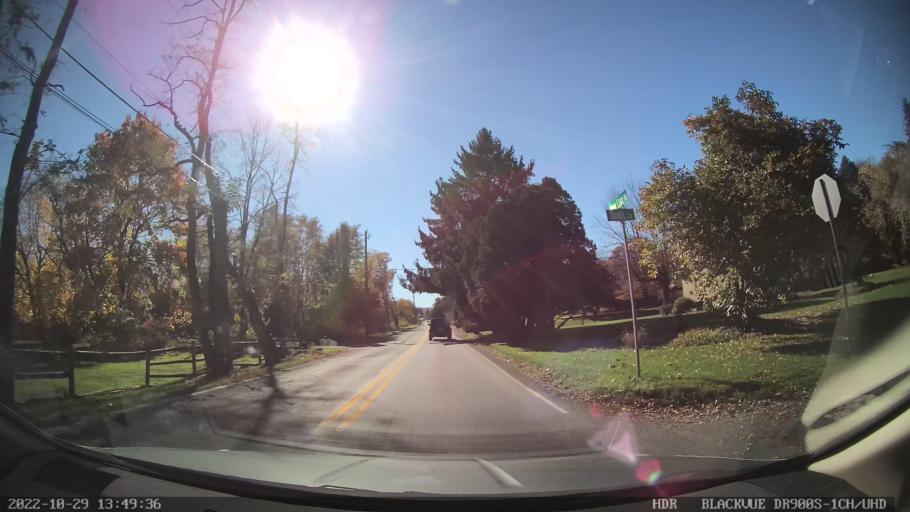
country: US
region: Pennsylvania
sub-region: Lehigh County
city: Emmaus
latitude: 40.5408
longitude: -75.4539
